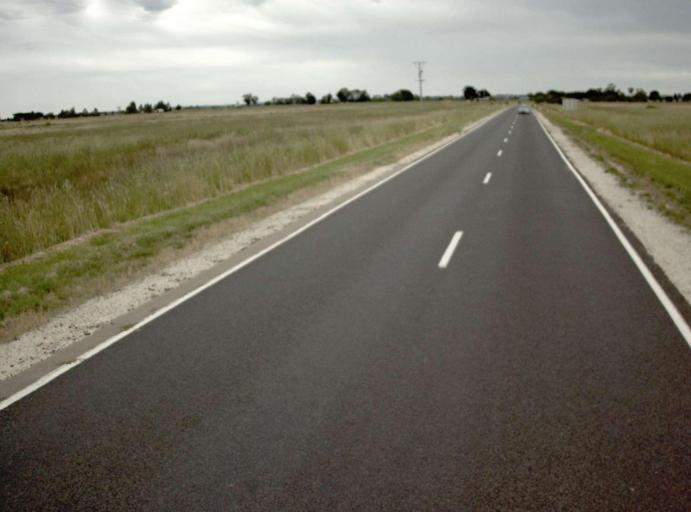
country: AU
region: Victoria
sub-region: Wellington
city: Sale
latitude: -38.0674
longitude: 147.1462
